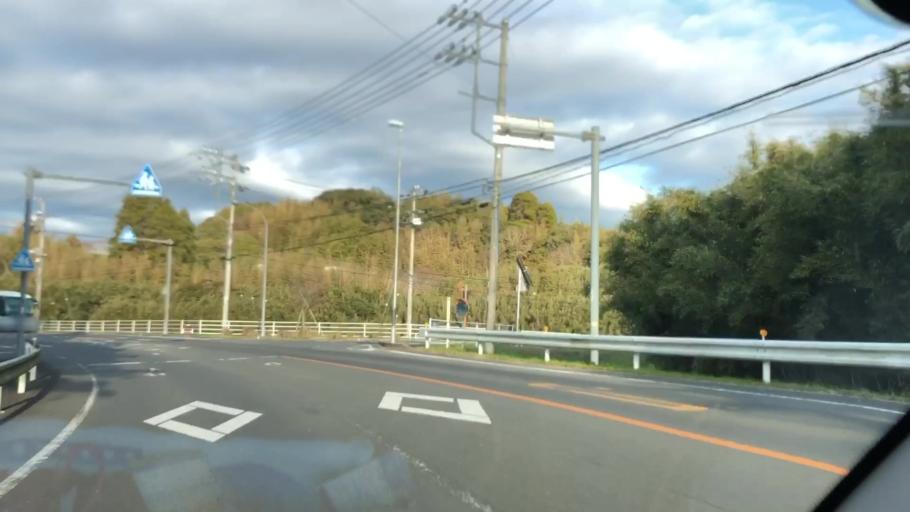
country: JP
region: Chiba
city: Tateyama
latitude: 34.9864
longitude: 139.9419
